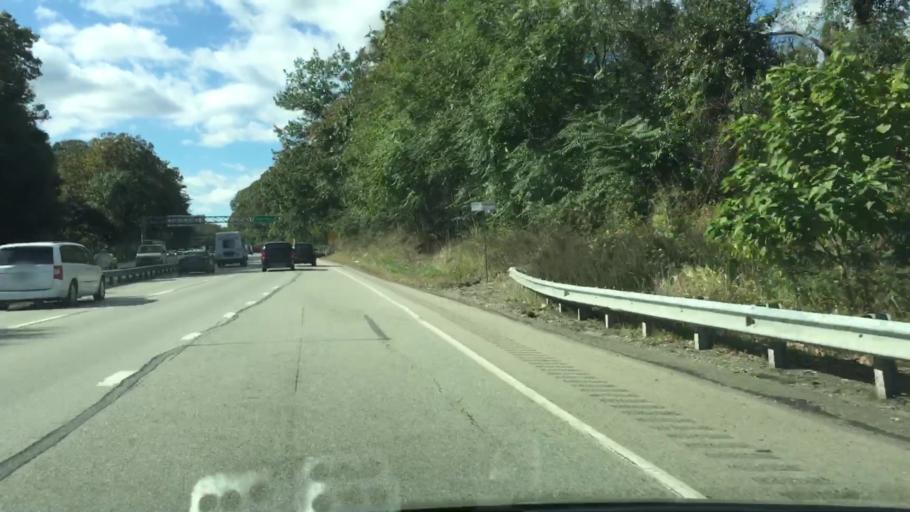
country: US
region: Pennsylvania
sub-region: Delaware County
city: Media
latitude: 39.9368
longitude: -75.3711
